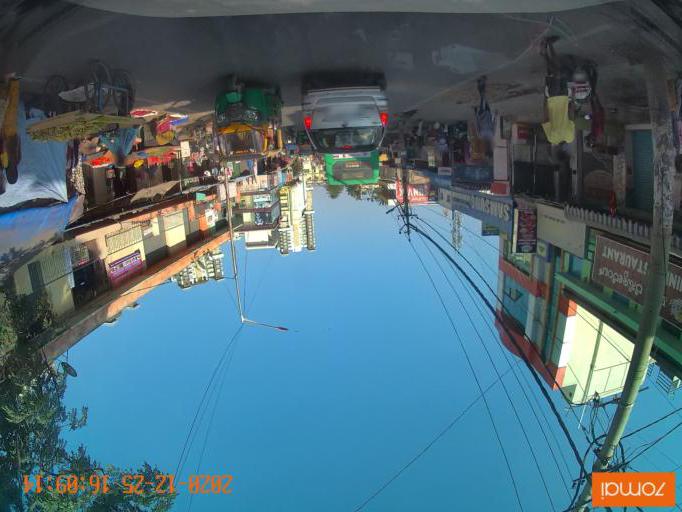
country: IN
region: Karnataka
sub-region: Bangalore Urban
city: Bangalore
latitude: 12.8994
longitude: 77.6267
